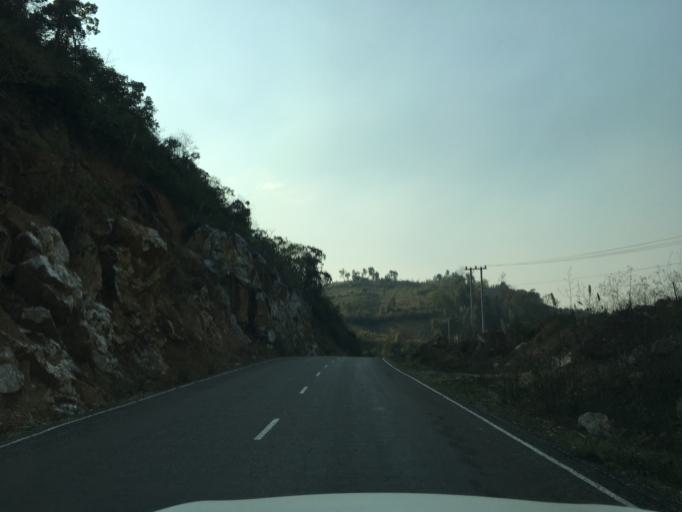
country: LA
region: Houaphan
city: Xam Nua
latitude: 20.5699
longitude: 104.0594
